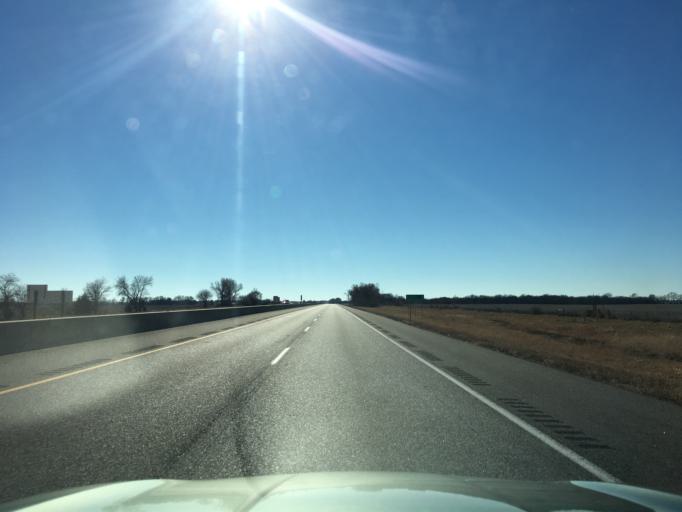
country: US
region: Kansas
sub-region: Sumner County
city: Mulvane
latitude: 37.4644
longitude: -97.3227
